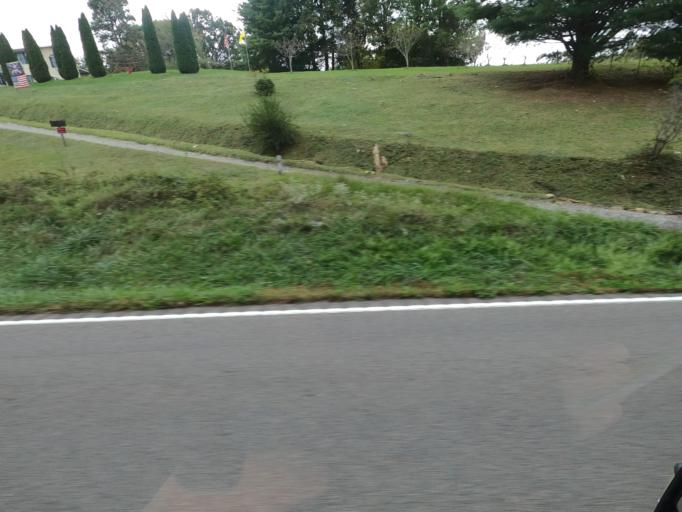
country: US
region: Tennessee
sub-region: Carter County
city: Elizabethton
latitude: 36.2607
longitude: -82.2238
